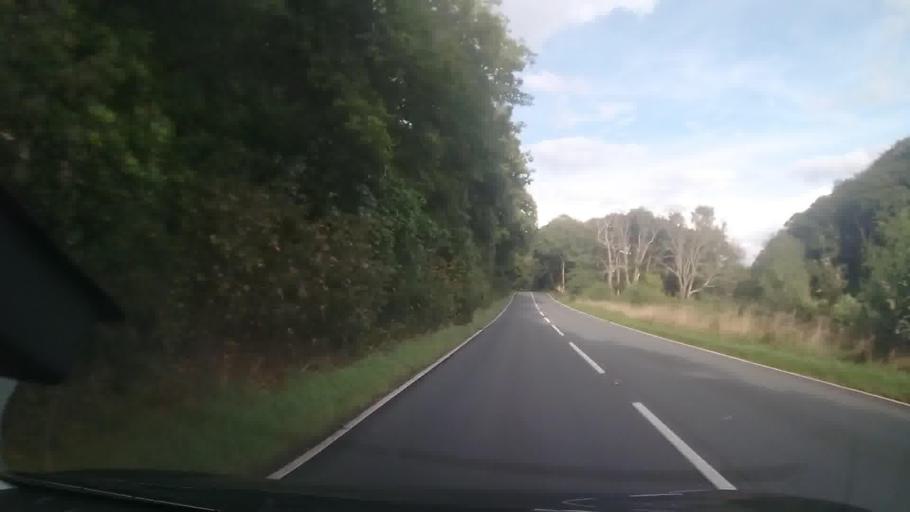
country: GB
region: Wales
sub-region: Gwynedd
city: Barmouth
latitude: 52.7409
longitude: -4.0105
